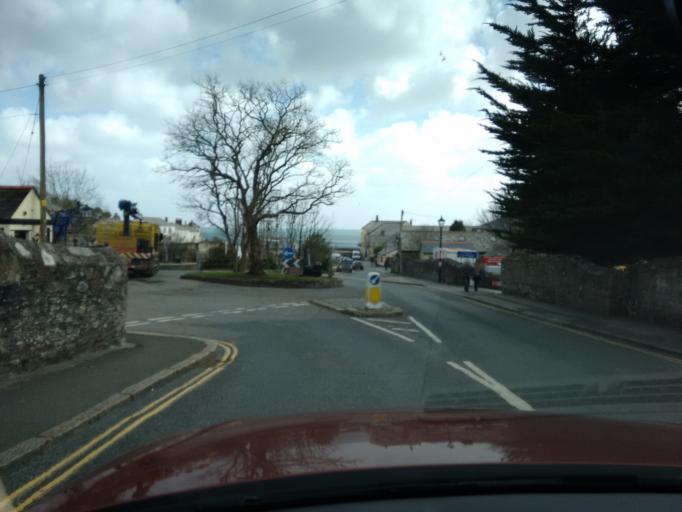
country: GB
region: England
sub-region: Cornwall
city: St Austell
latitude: 50.3327
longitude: -4.7581
